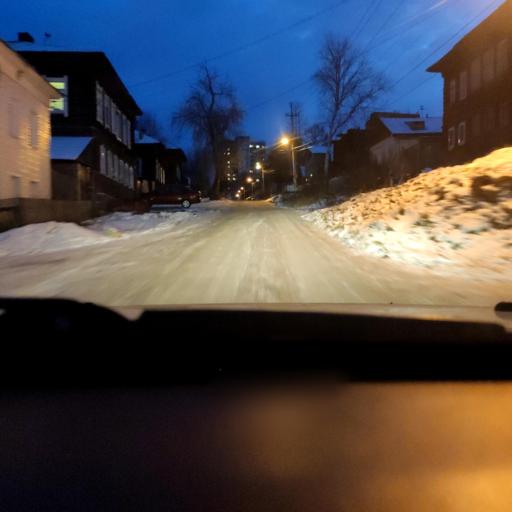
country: RU
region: Perm
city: Perm
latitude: 58.0369
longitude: 56.3236
